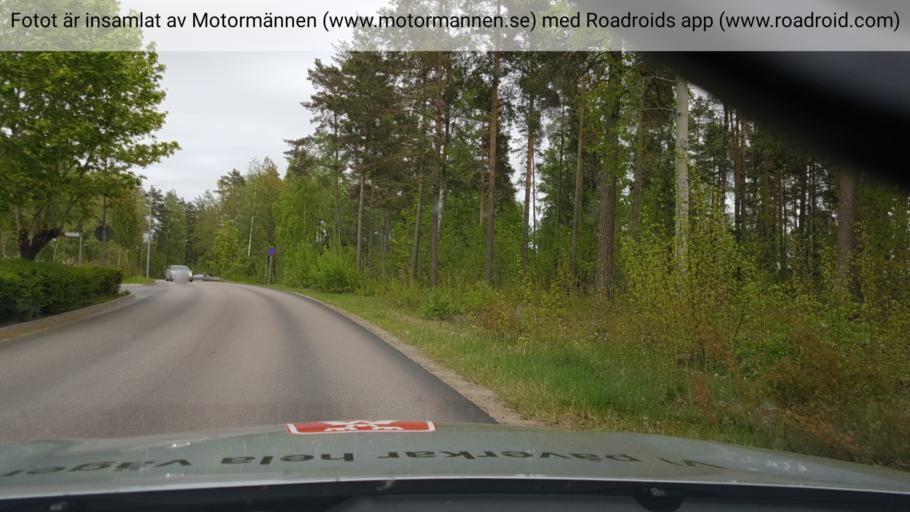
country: SE
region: Vaestmanland
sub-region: Vasteras
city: Vasteras
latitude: 59.6391
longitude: 16.5450
